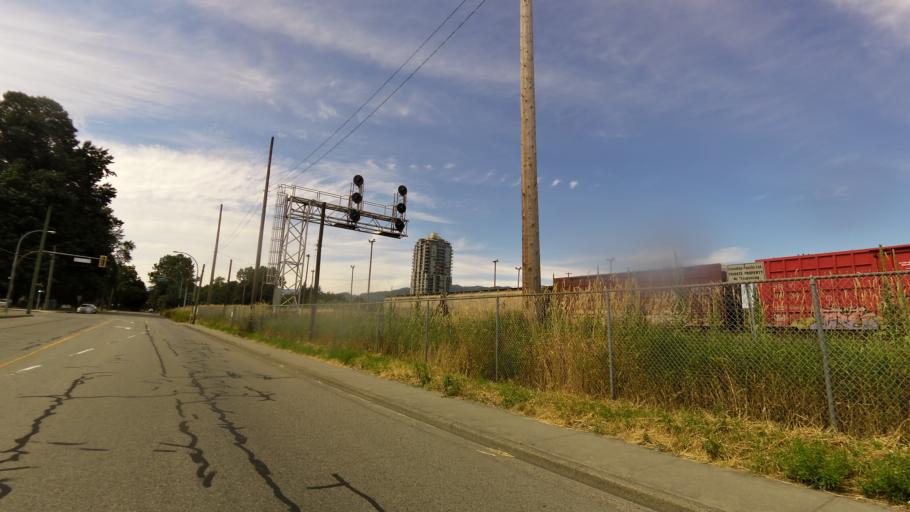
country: CA
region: British Columbia
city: Coquitlam
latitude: 49.2629
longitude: -122.7762
